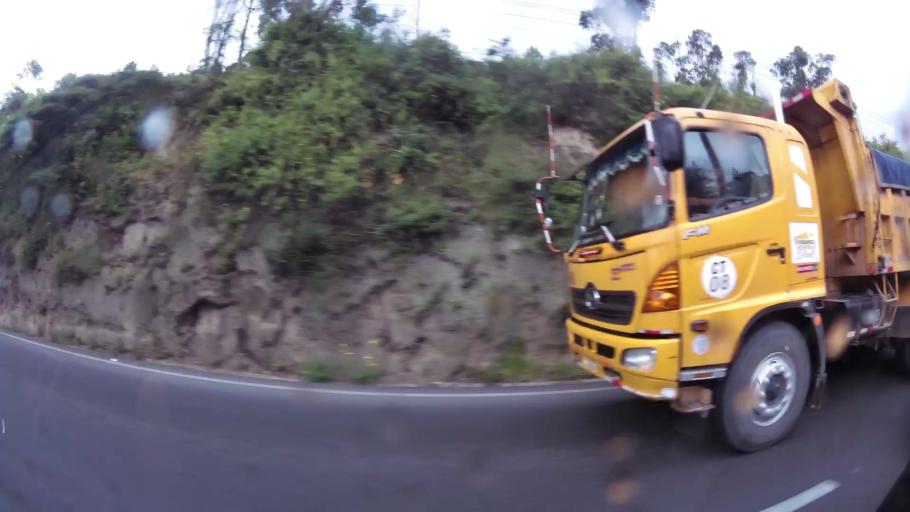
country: EC
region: Pichincha
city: Quito
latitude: -0.0836
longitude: -78.4838
